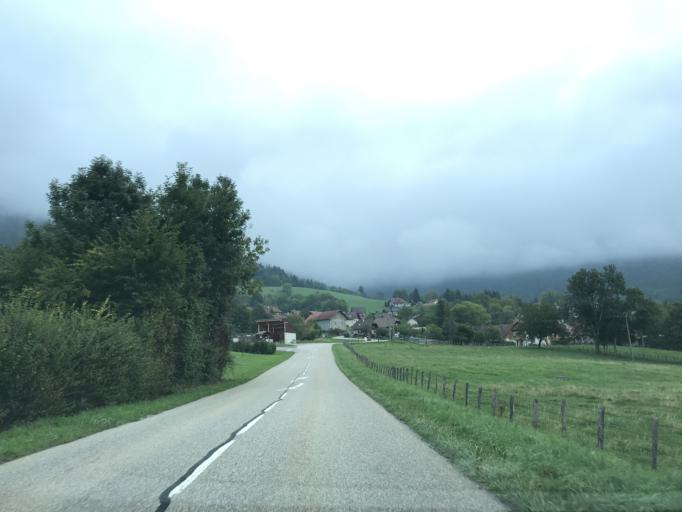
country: FR
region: Rhone-Alpes
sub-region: Departement de la Haute-Savoie
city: Talloires
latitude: 45.8382
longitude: 6.2278
